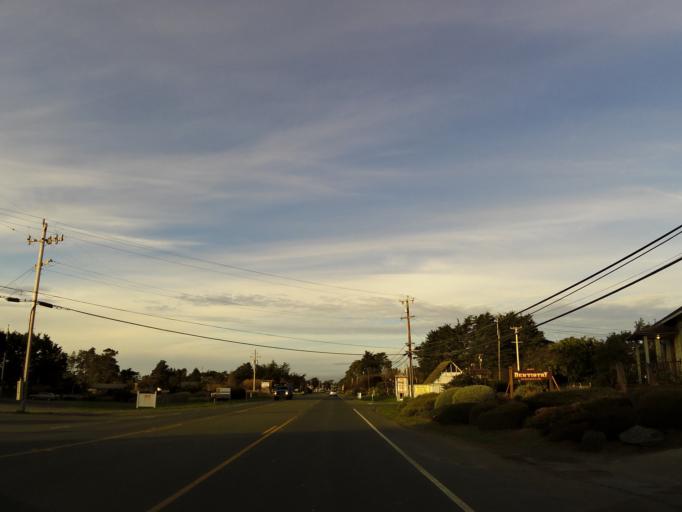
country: US
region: California
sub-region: Mendocino County
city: Fort Bragg
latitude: 39.4078
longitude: -123.8087
